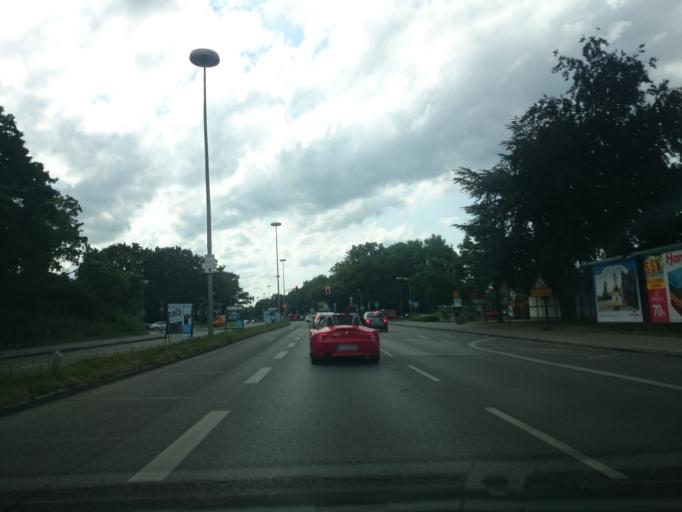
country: DE
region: Bavaria
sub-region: Swabia
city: Stadtbergen
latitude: 48.3717
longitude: 10.8714
